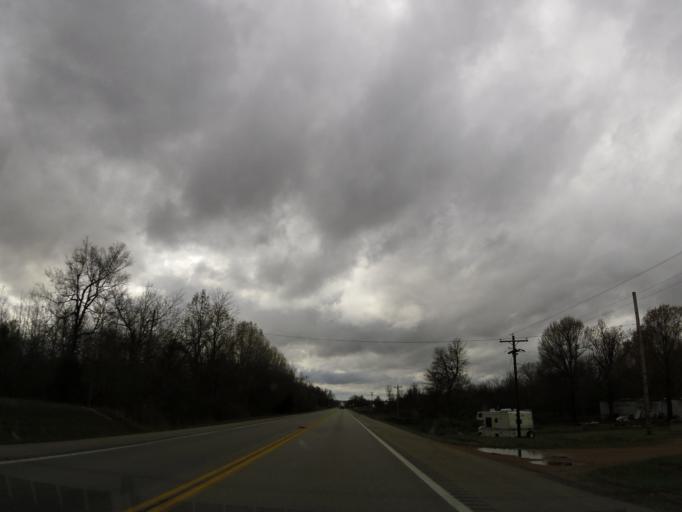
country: US
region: Missouri
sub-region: Butler County
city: Poplar Bluff
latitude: 36.6541
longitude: -90.5201
